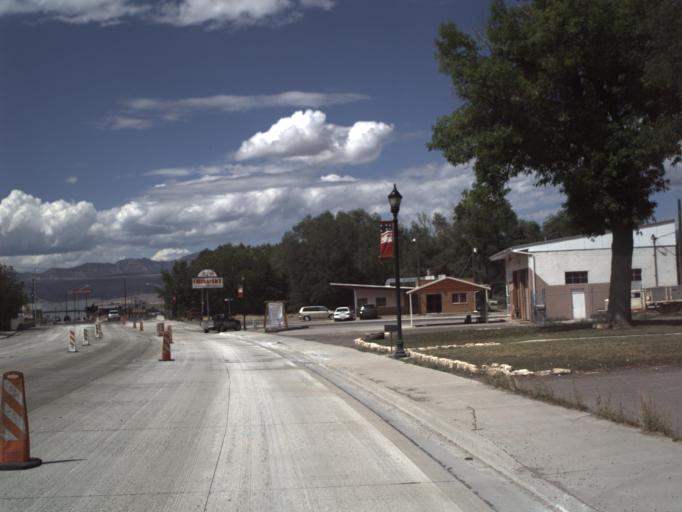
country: US
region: Utah
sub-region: Sevier County
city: Salina
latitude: 38.9577
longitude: -111.8629
